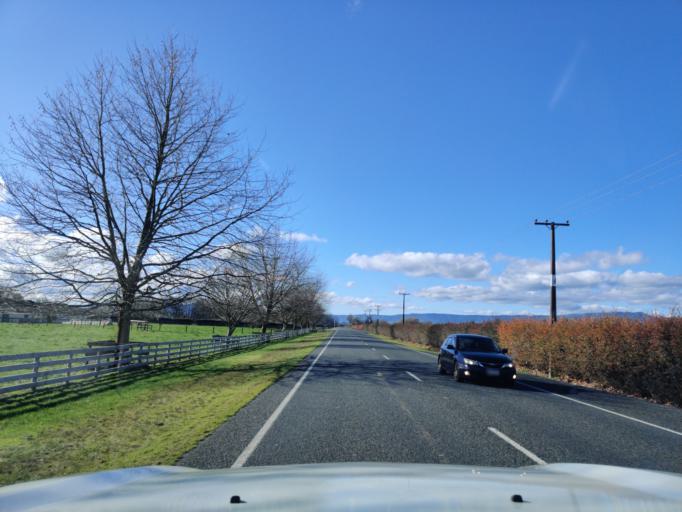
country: NZ
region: Waikato
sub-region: Matamata-Piako District
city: Matamata
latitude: -37.8721
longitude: 175.7447
